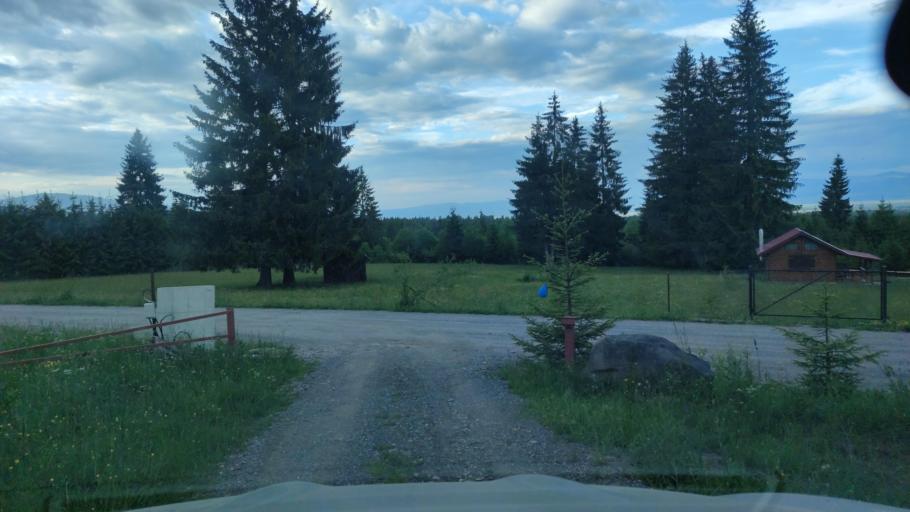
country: RO
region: Harghita
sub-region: Comuna Joseni
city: Joseni
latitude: 46.6639
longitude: 25.3847
